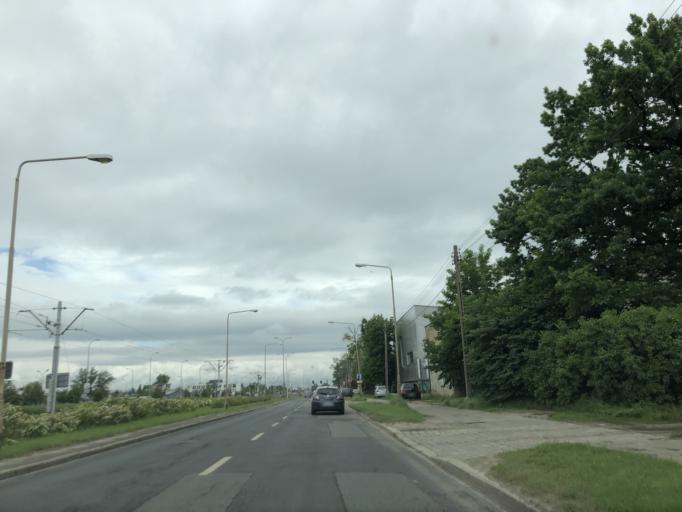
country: PL
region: Lower Silesian Voivodeship
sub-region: Powiat wroclawski
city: Wroclaw
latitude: 51.1422
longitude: 17.0320
